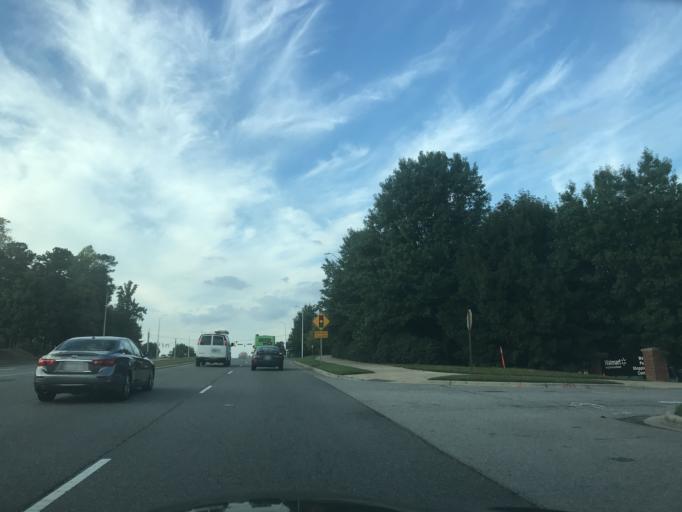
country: US
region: North Carolina
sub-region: Wake County
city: Green Level
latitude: 35.7855
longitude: -78.8710
